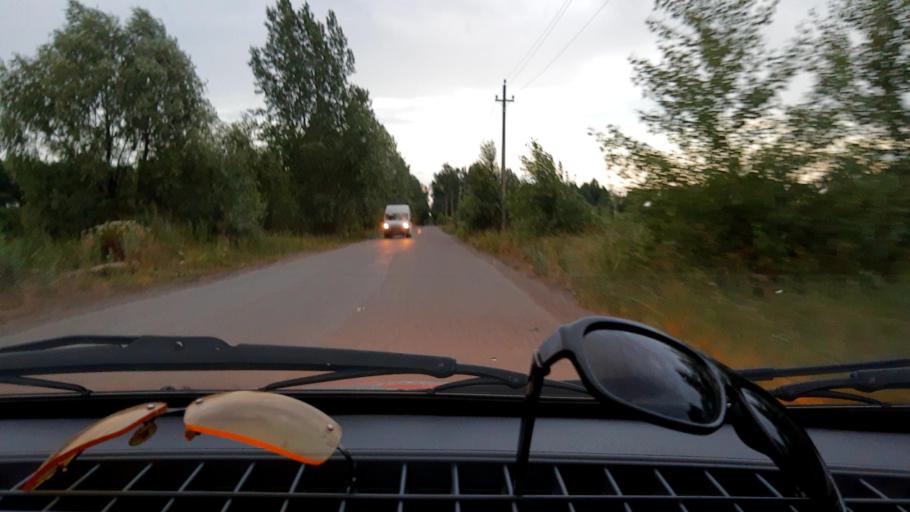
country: RU
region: Bashkortostan
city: Avdon
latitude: 54.6644
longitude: 55.8228
